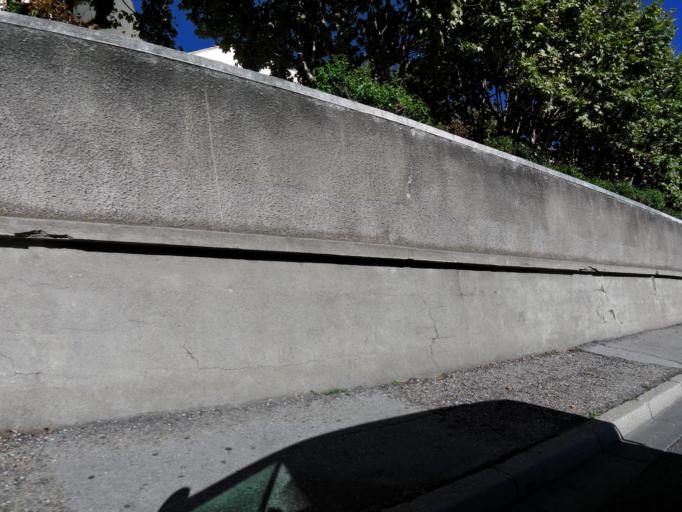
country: FR
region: Languedoc-Roussillon
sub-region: Departement du Gard
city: Nimes
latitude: 43.8236
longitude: 4.3638
